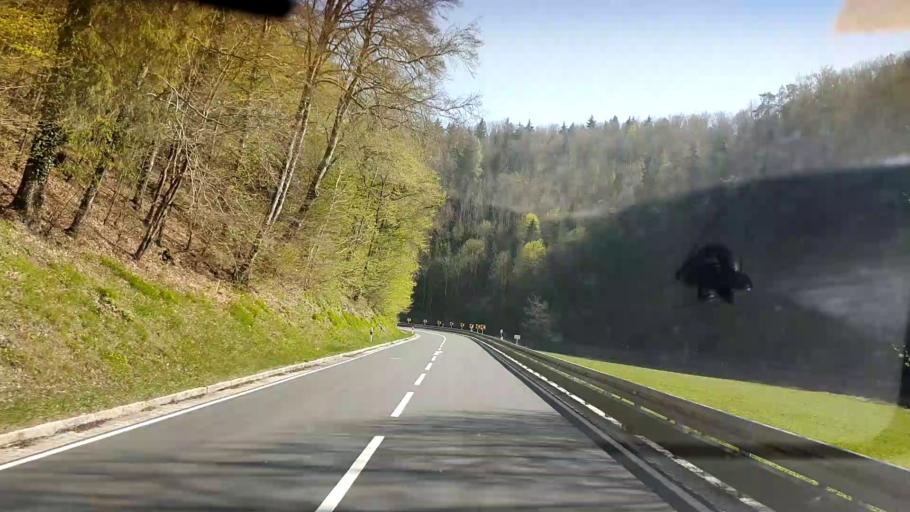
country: DE
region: Bavaria
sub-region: Upper Franconia
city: Gossweinstein
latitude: 49.7754
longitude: 11.2967
